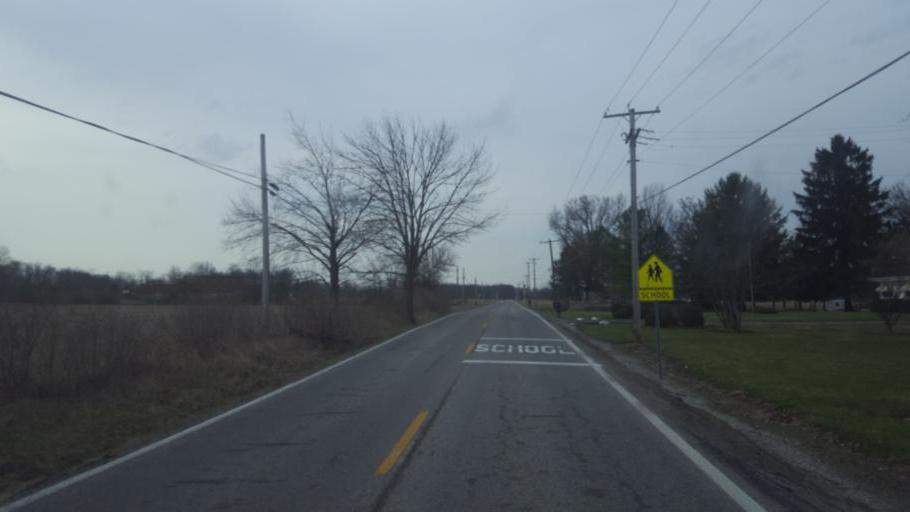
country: US
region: Ohio
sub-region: Morrow County
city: Cardington
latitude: 40.6289
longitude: -82.9674
